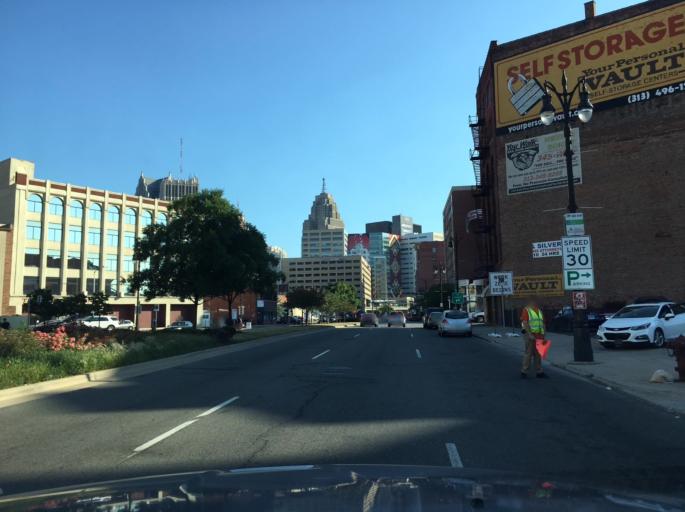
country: US
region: Michigan
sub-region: Wayne County
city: Detroit
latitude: 42.3369
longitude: -83.0440
